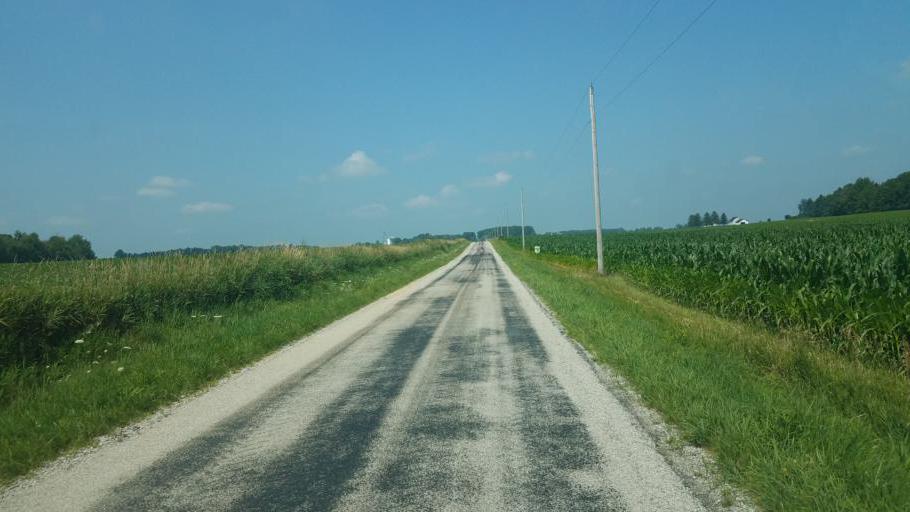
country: US
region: Ohio
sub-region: Huron County
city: Willard
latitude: 40.9800
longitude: -82.8596
